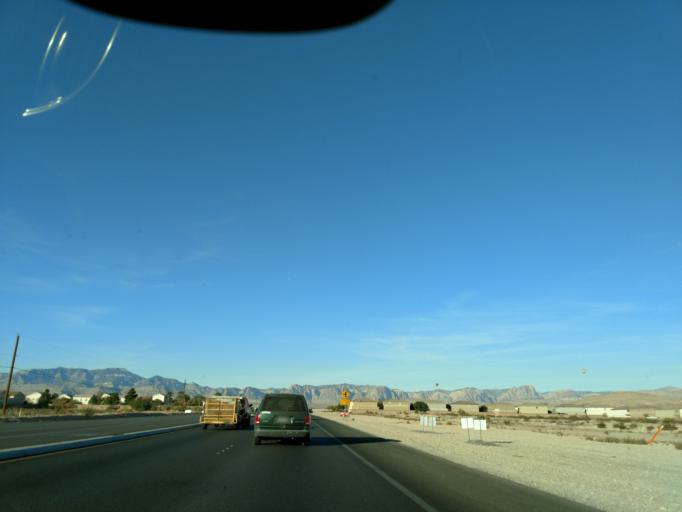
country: US
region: Nevada
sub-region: Clark County
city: Enterprise
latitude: 36.0204
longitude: -115.2818
